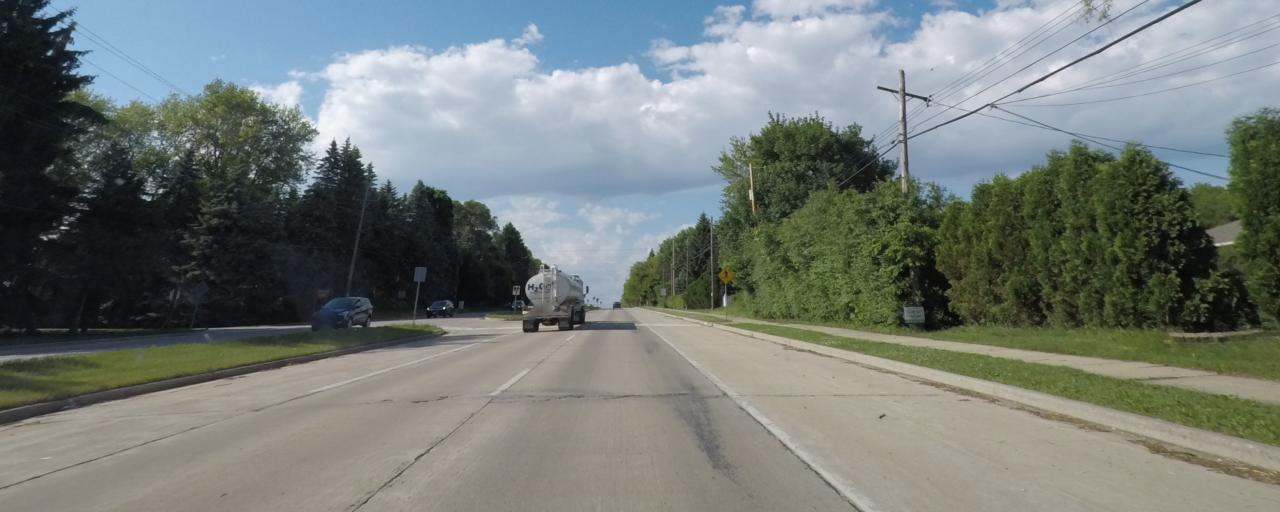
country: US
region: Wisconsin
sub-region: Milwaukee County
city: Greendale
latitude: 42.9345
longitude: -88.0084
